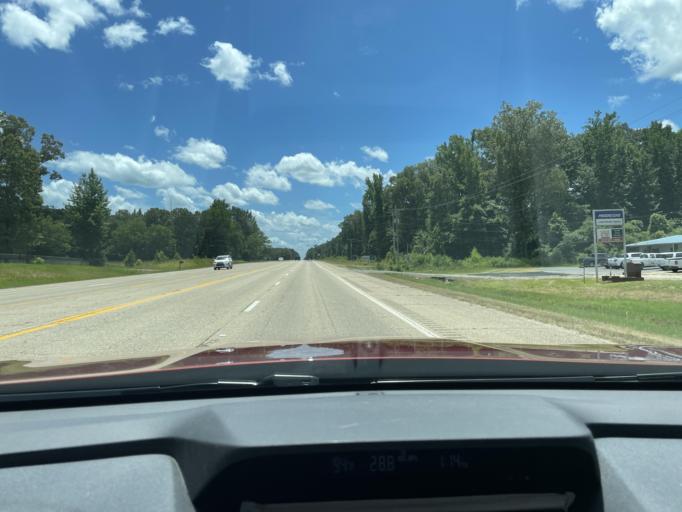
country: US
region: Arkansas
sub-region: Drew County
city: Monticello
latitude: 33.6641
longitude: -91.8036
